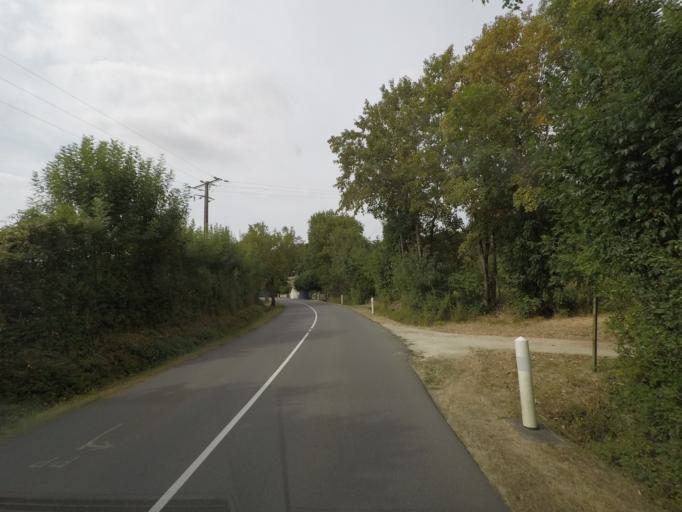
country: FR
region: Poitou-Charentes
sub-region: Departement de la Charente
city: Nanteuil-en-Vallee
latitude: 46.0013
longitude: 0.3195
